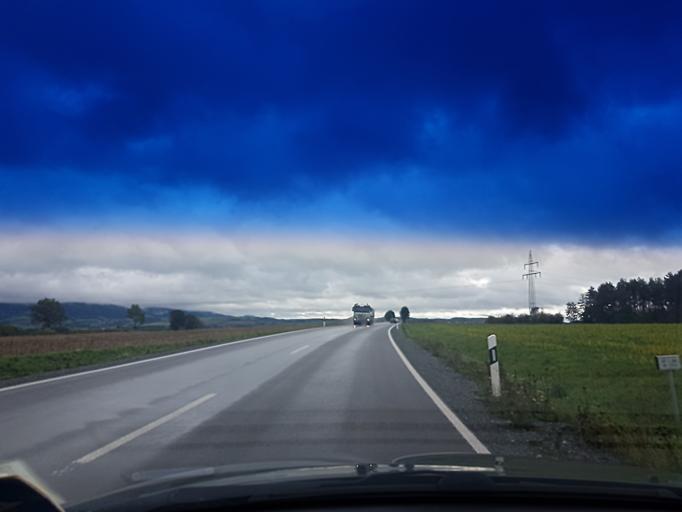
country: DE
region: Bavaria
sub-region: Upper Franconia
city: Bindlach
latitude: 50.0140
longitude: 11.6107
